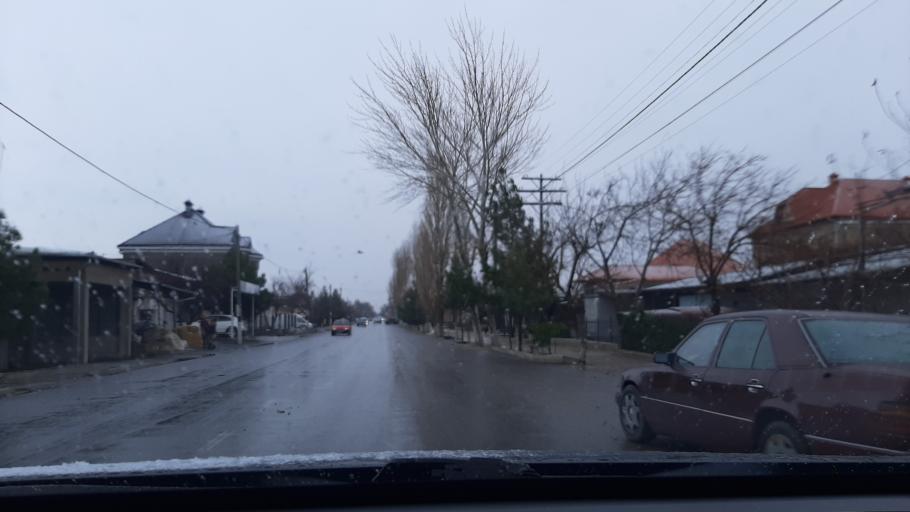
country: TJ
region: Viloyati Sughd
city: Khujand
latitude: 40.2683
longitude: 69.6236
